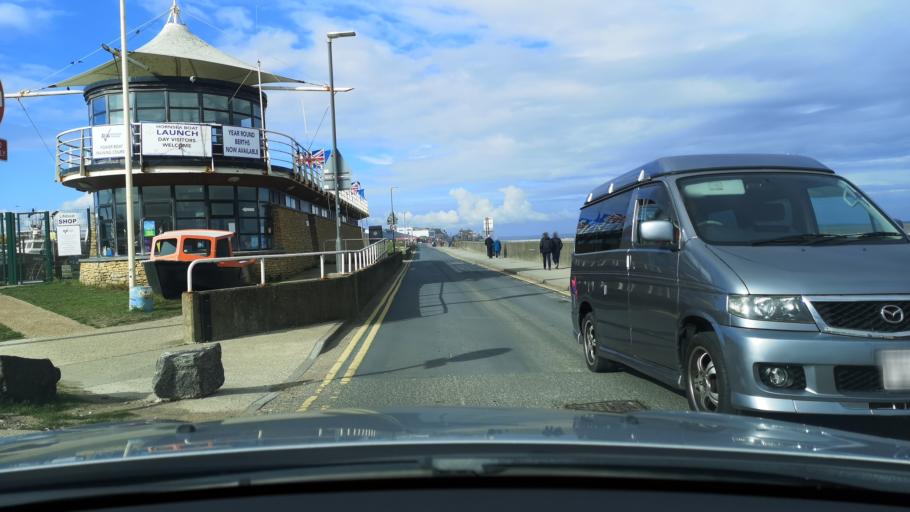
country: GB
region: England
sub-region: East Riding of Yorkshire
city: Hornsea
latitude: 53.9084
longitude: -0.1581
